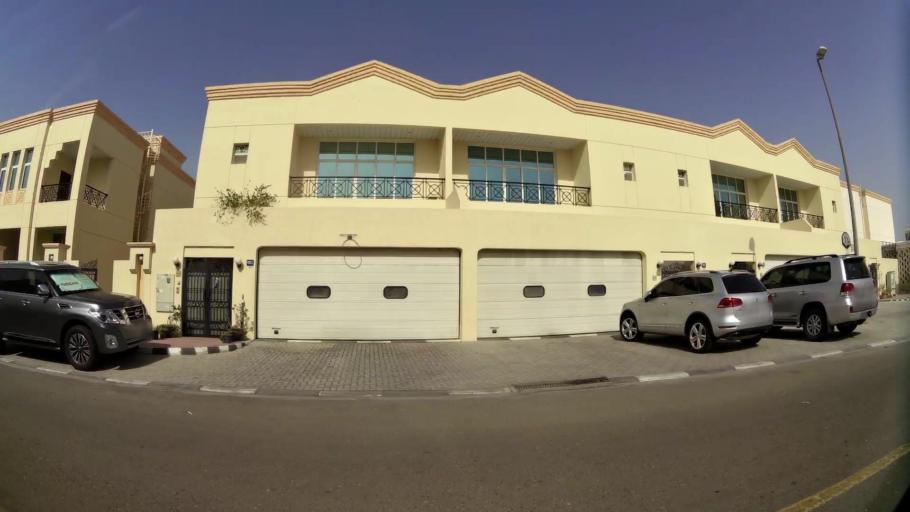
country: AE
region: Ash Shariqah
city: Sharjah
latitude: 25.2446
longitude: 55.3496
